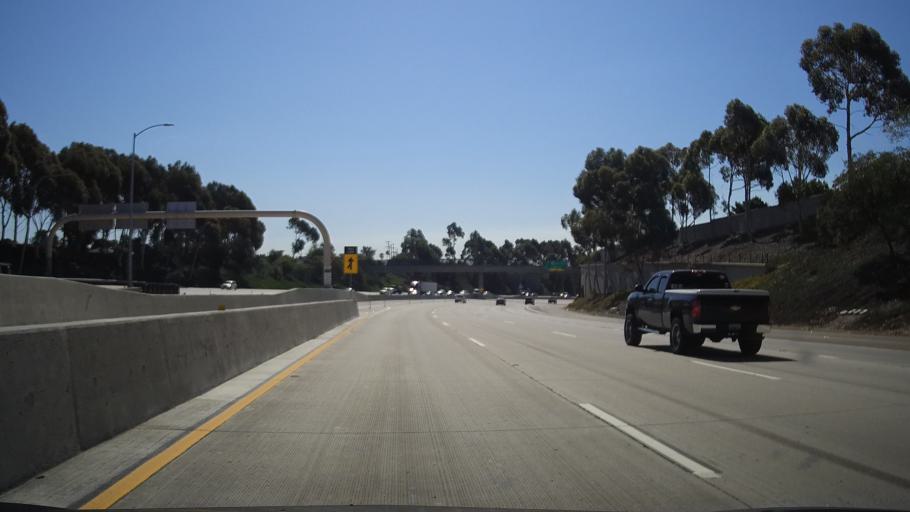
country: US
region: California
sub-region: San Diego County
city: San Diego
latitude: 32.7474
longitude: -117.1085
